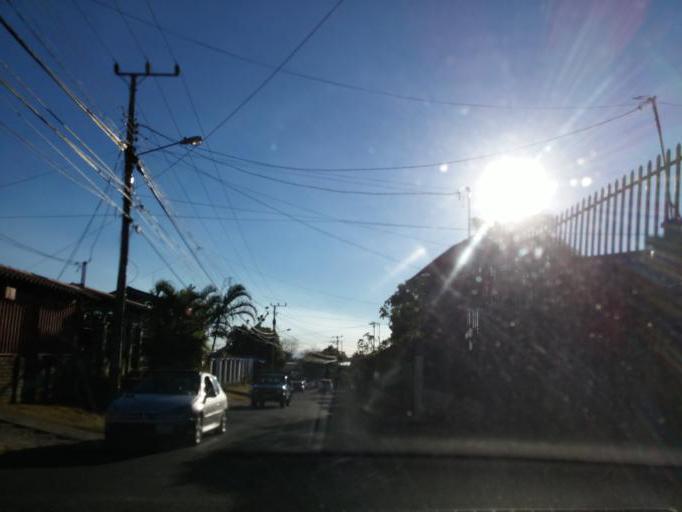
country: CR
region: Heredia
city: Llorente
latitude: 10.0080
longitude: -84.1754
